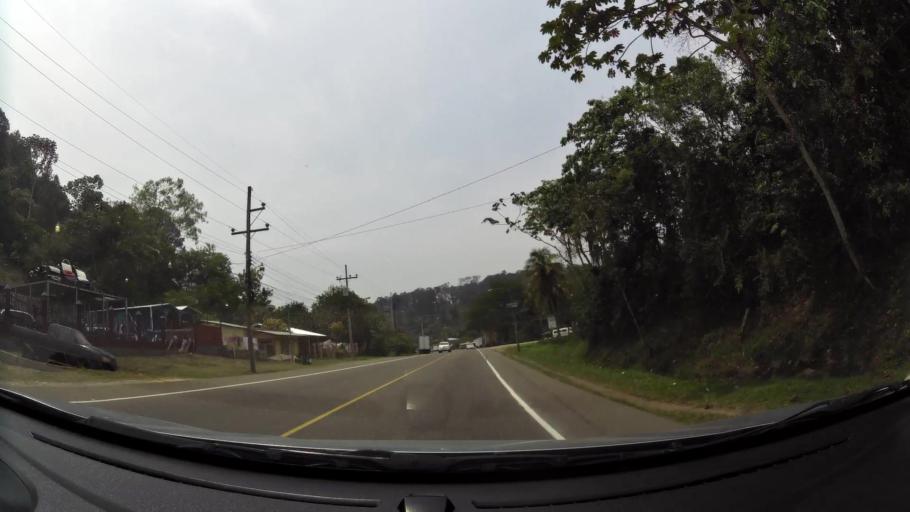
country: HN
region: Cortes
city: La Guama
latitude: 14.8874
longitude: -87.9381
